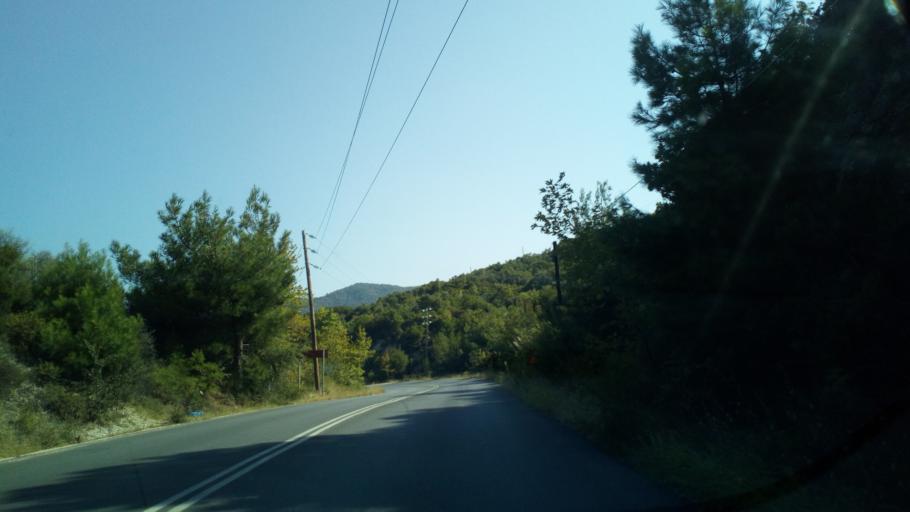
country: GR
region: Central Macedonia
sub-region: Nomos Chalkidikis
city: Stratonion
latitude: 40.5895
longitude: 23.7922
